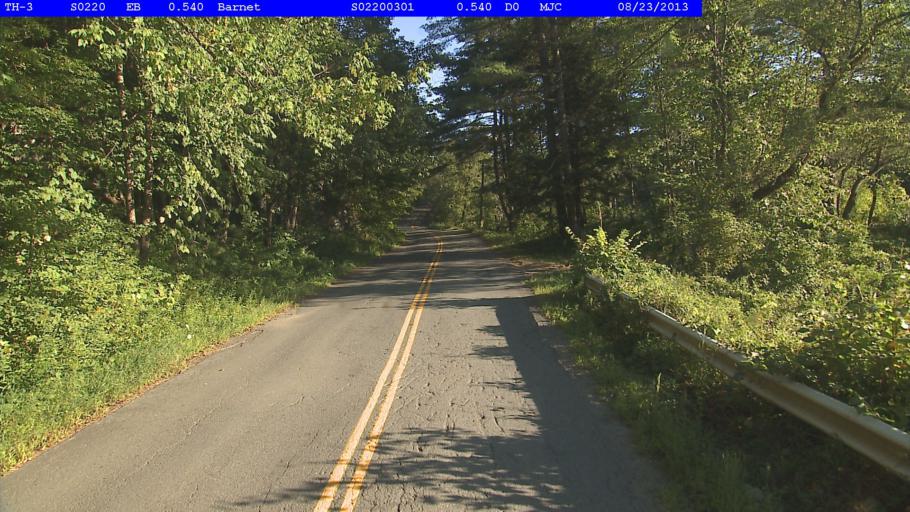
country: US
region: Vermont
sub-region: Caledonia County
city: Saint Johnsbury
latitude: 44.3260
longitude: -72.0335
